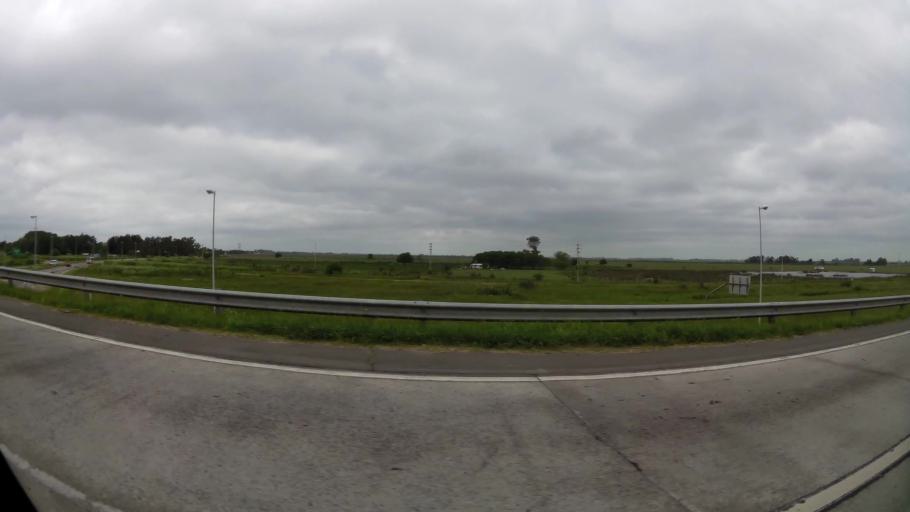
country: AR
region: Buenos Aires
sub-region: Partido de San Vicente
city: San Vicente
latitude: -35.0257
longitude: -58.3485
